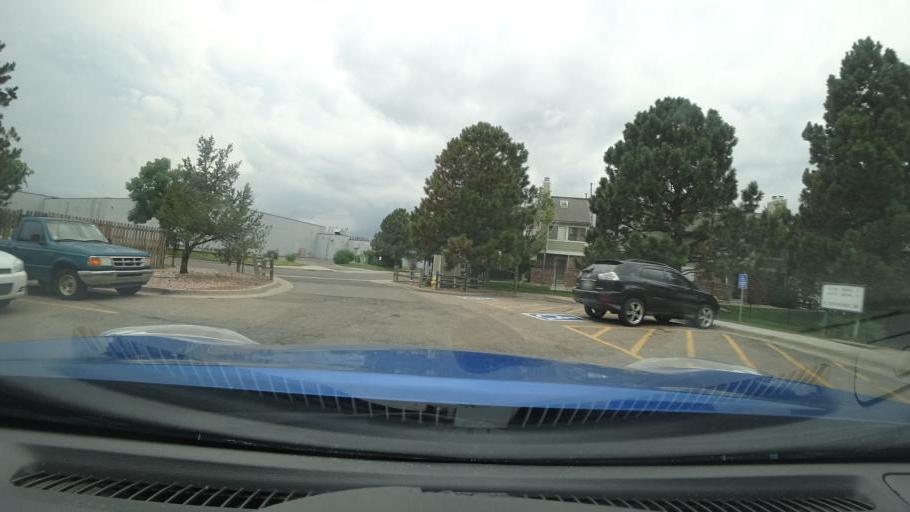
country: US
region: Colorado
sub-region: Adams County
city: Aurora
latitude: 39.6987
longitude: -104.8166
